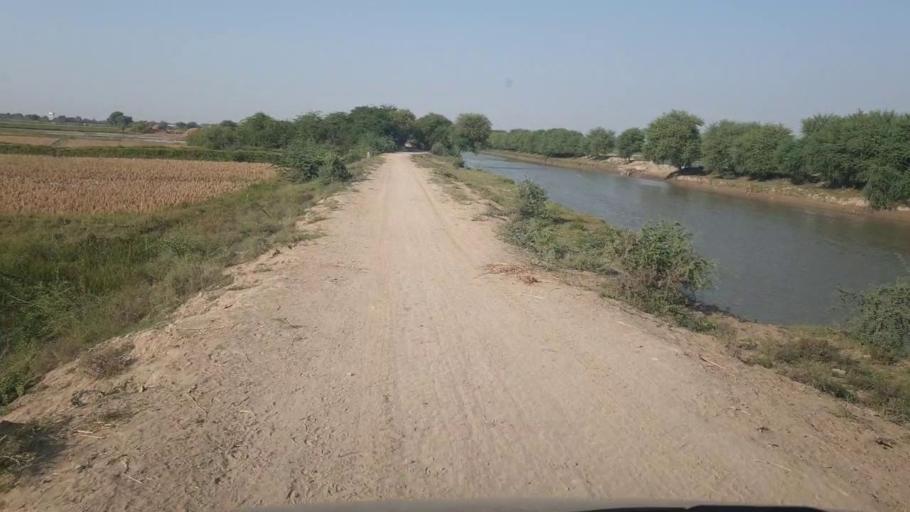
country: PK
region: Sindh
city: Badin
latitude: 24.6395
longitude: 68.8150
